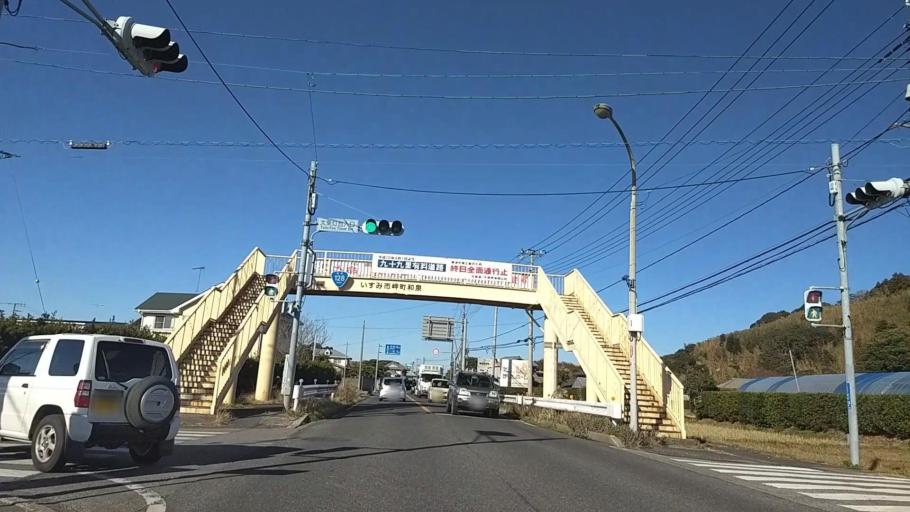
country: JP
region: Chiba
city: Ohara
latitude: 35.3119
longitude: 140.4026
